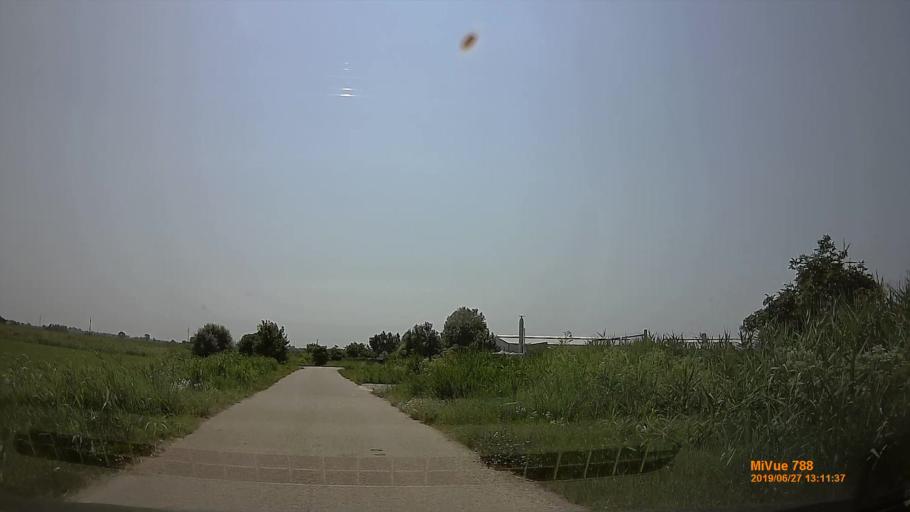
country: HU
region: Pest
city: Cegled
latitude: 47.1926
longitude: 19.8303
